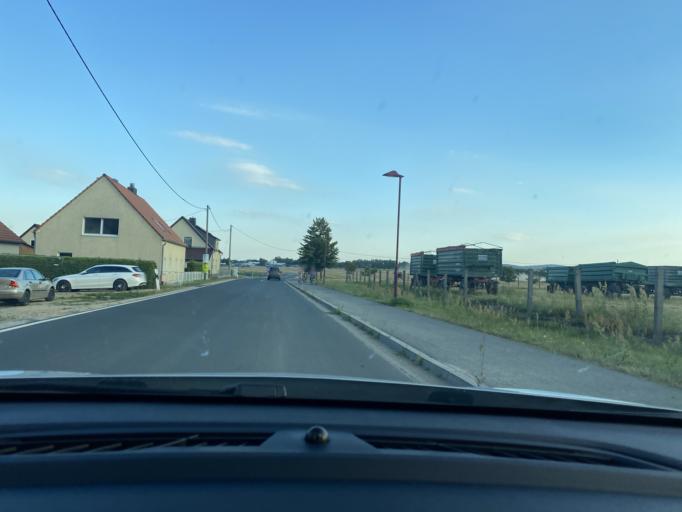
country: DE
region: Saxony
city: Kodersdorf
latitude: 51.2558
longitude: 14.8876
